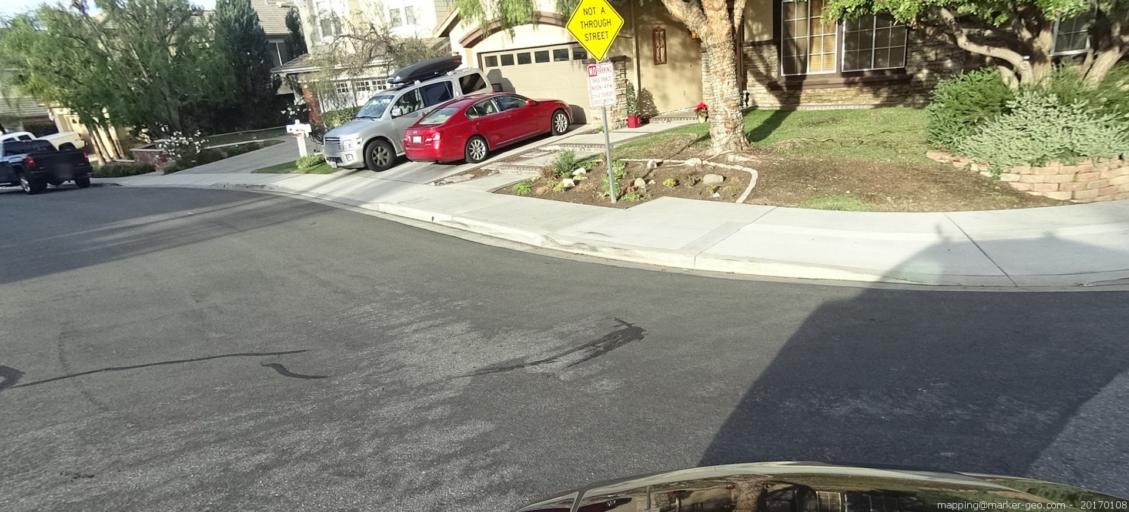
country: US
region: California
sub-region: Orange County
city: Las Flores
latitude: 33.5905
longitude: -117.6212
